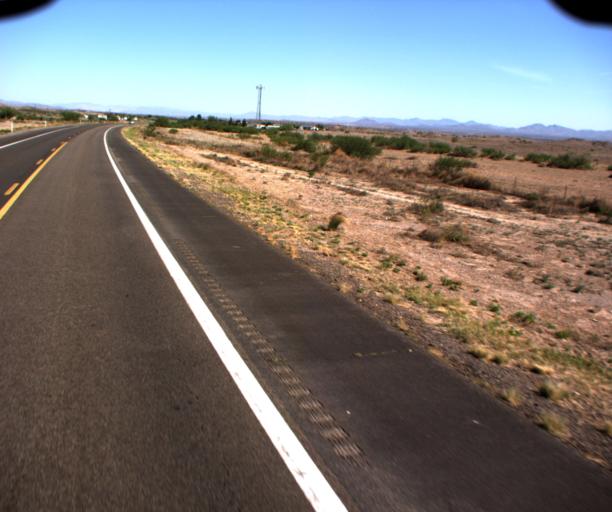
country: US
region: Arizona
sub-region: Greenlee County
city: Clifton
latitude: 32.6628
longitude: -109.0723
